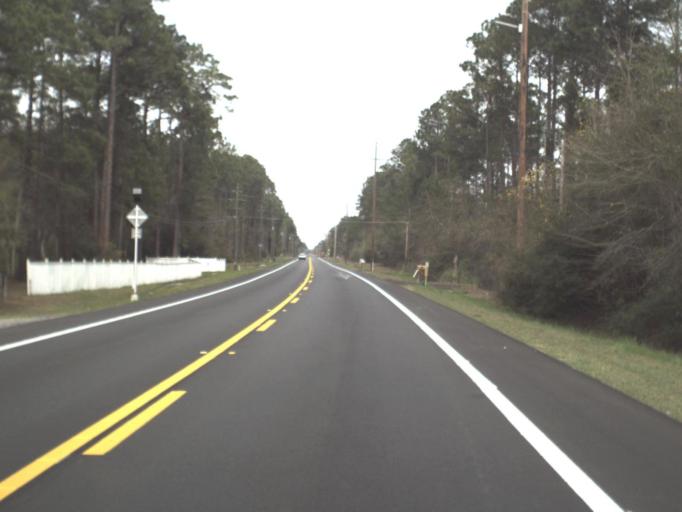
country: US
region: Florida
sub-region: Gadsden County
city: Midway
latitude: 30.4061
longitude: -84.5616
